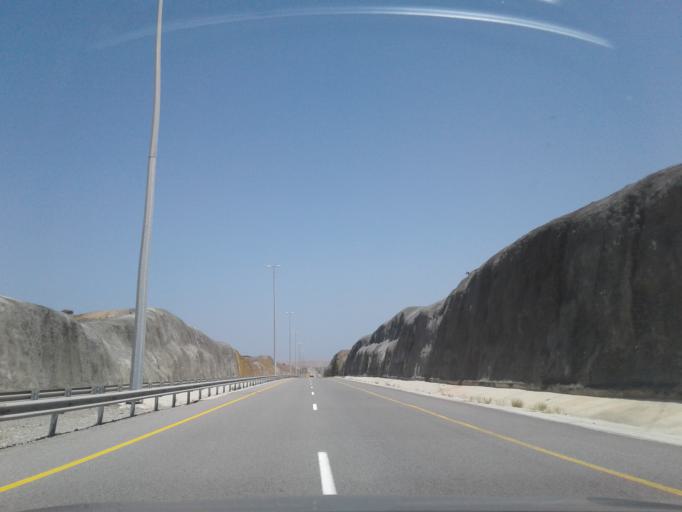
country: OM
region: Muhafazat Masqat
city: Muscat
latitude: 23.1914
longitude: 58.8443
